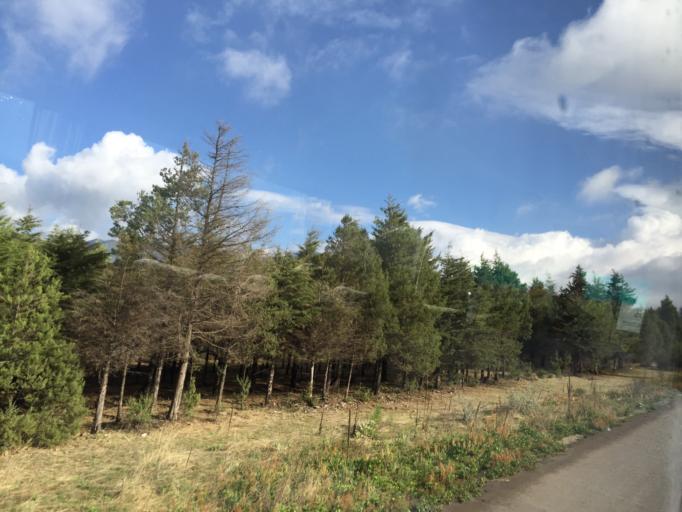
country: CN
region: Yunnan
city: Lijiang
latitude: 26.9479
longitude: 100.2315
